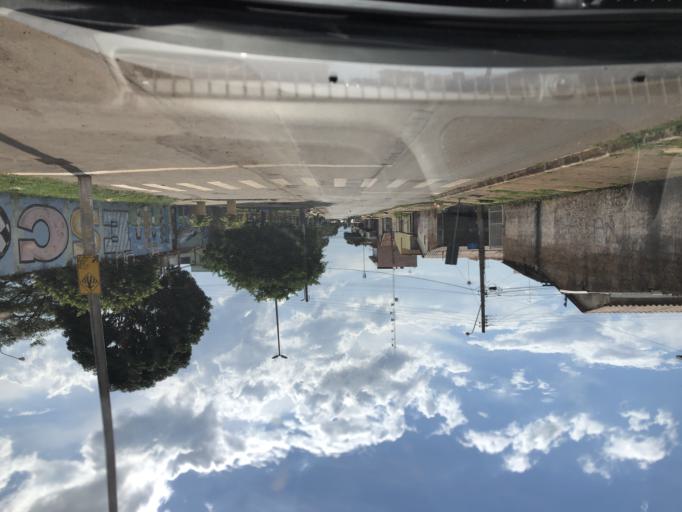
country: BR
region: Federal District
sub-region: Brasilia
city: Brasilia
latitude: -15.7910
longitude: -48.1210
